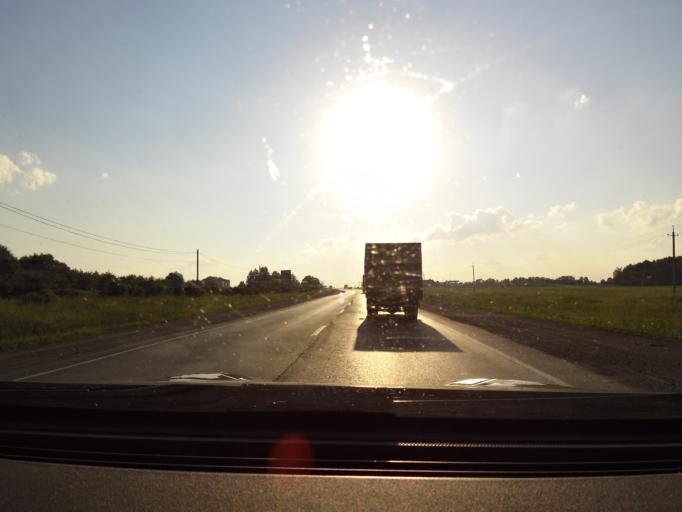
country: RU
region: Sverdlovsk
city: Druzhinino
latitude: 56.8101
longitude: 59.5350
